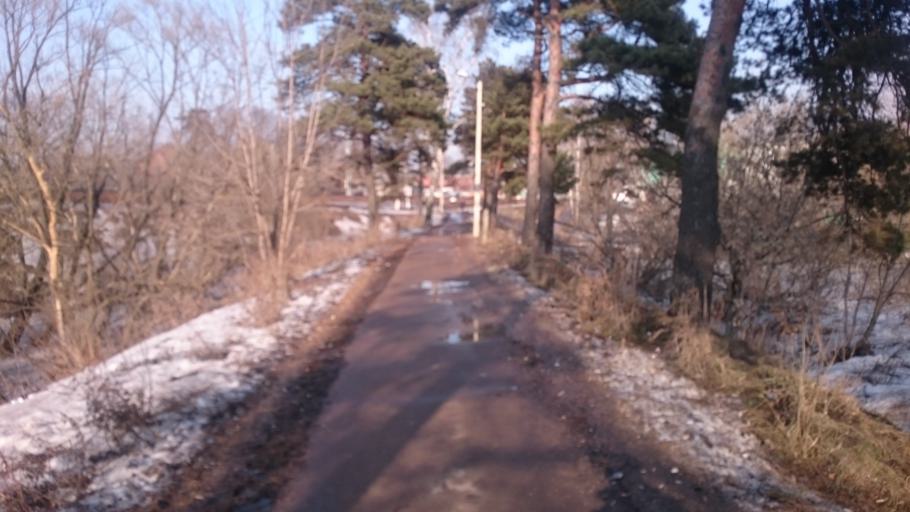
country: RU
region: Moskovskaya
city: Novoivanovskoye
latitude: 55.7137
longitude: 37.3708
